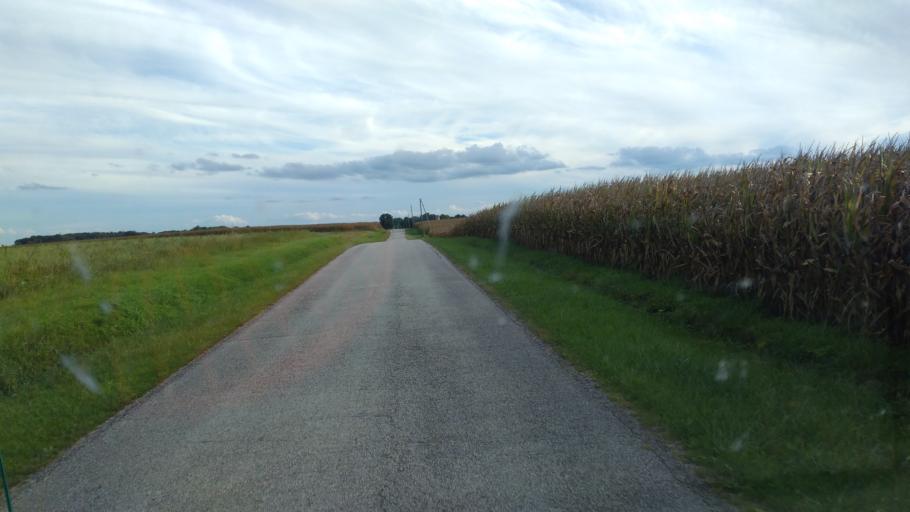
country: US
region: Ohio
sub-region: Crawford County
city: Bucyrus
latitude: 40.8669
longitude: -82.9164
